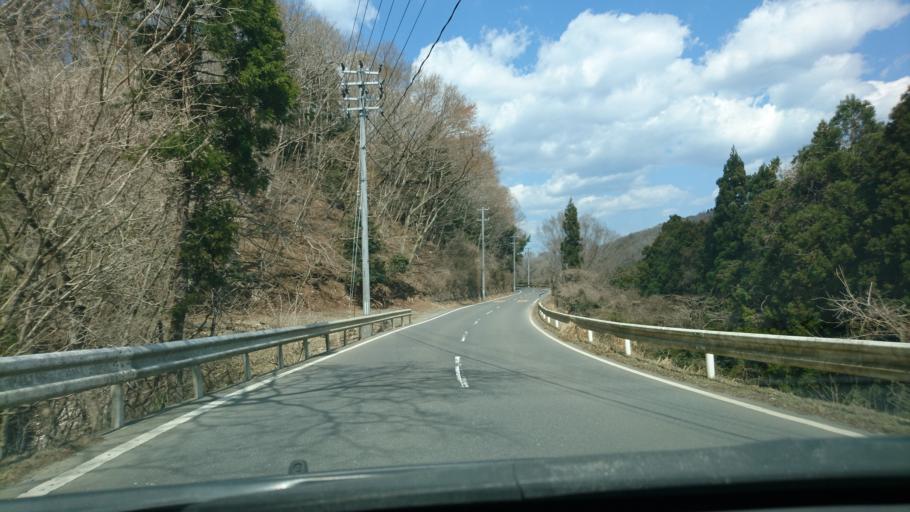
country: JP
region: Miyagi
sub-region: Oshika Gun
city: Onagawa Cho
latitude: 38.4579
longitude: 141.4865
